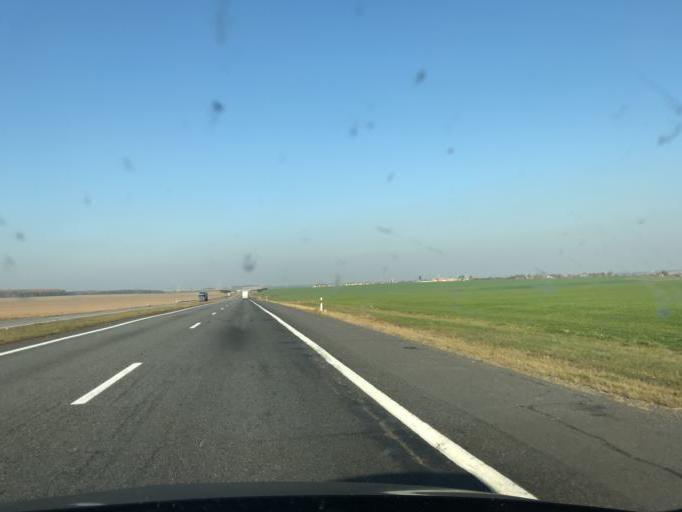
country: BY
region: Grodnenskaya
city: Mir
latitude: 53.4250
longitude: 26.5802
